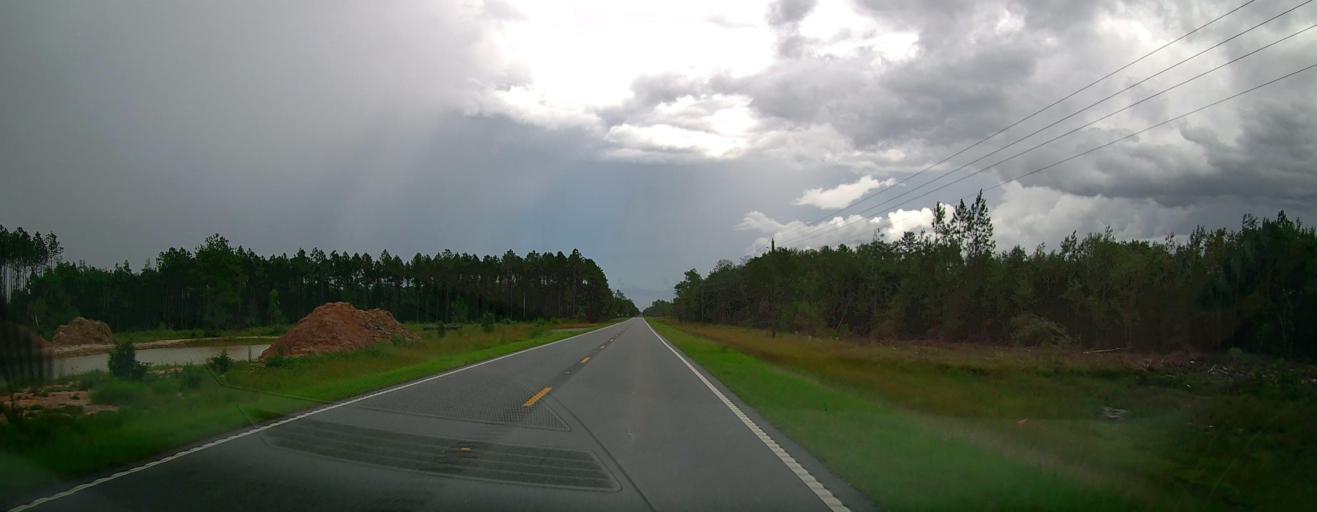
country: US
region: Georgia
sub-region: Pierce County
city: Blackshear
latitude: 31.3679
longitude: -82.0937
